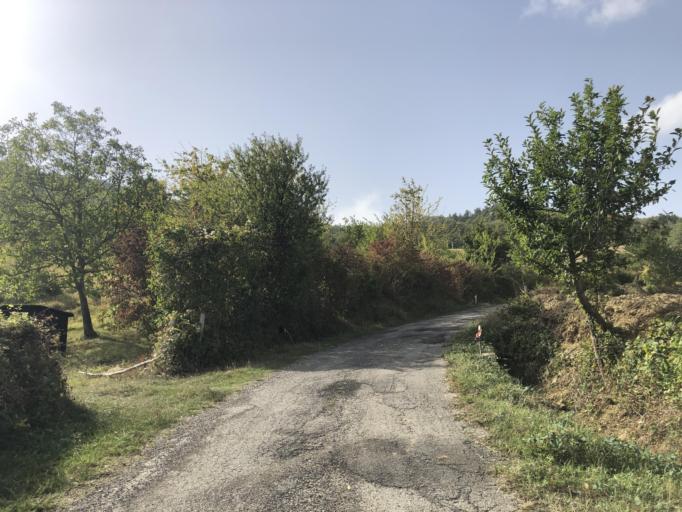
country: IT
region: Emilia-Romagna
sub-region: Forli-Cesena
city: Portico e San Benedetto
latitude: 44.0189
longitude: 11.7900
